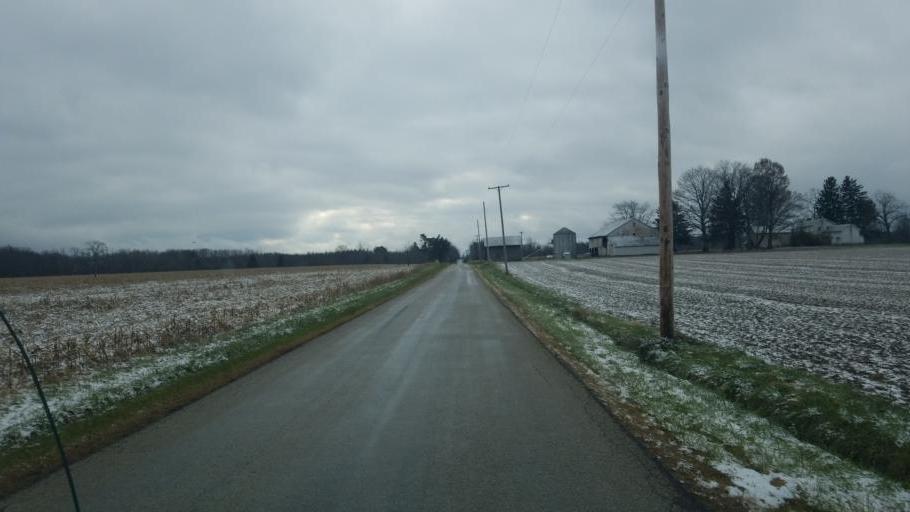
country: US
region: Ohio
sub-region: Richland County
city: Shelby
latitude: 40.8768
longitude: -82.5521
